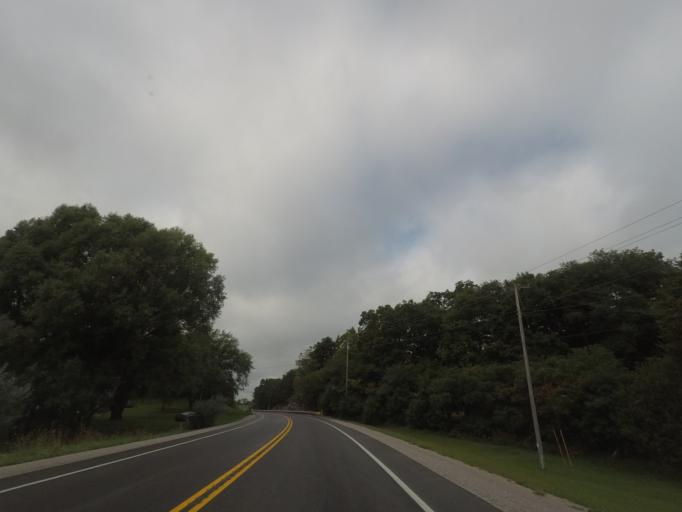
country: US
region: Wisconsin
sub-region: Jefferson County
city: Jefferson
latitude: 43.0125
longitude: -88.7616
